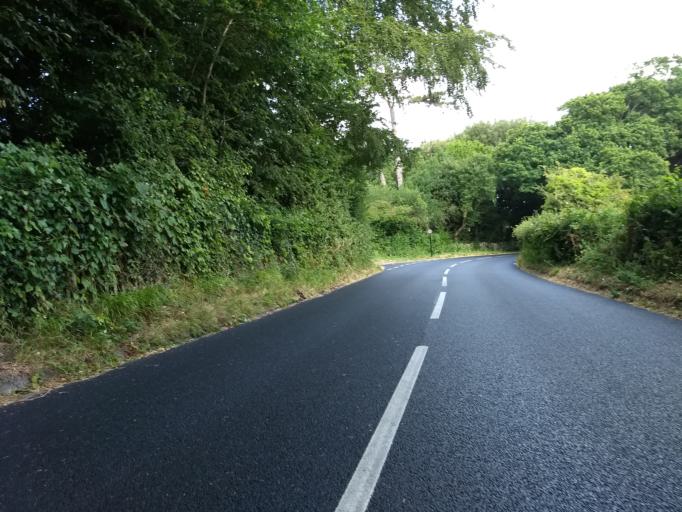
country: GB
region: England
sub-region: Isle of Wight
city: Bembridge
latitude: 50.6807
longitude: -1.0885
